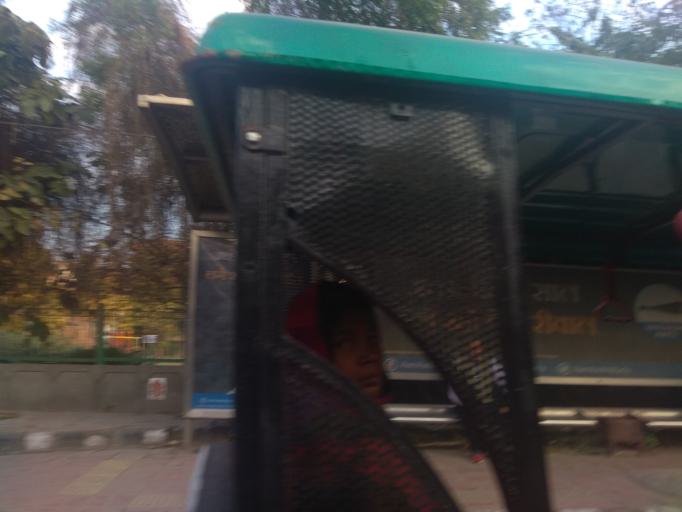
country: IN
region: NCT
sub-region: West Delhi
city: Nangloi Jat
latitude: 28.6332
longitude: 77.0688
